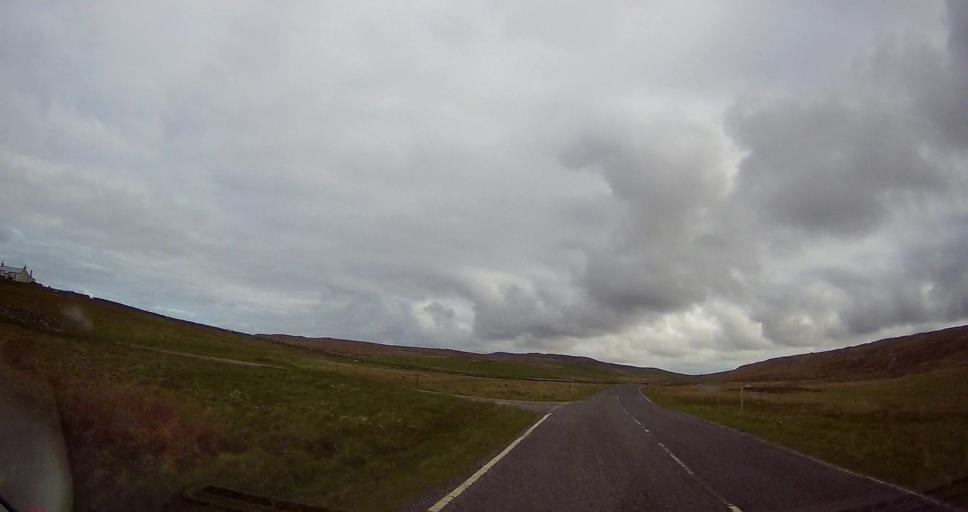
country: GB
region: Scotland
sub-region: Shetland Islands
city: Shetland
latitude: 60.6863
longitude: -0.9644
